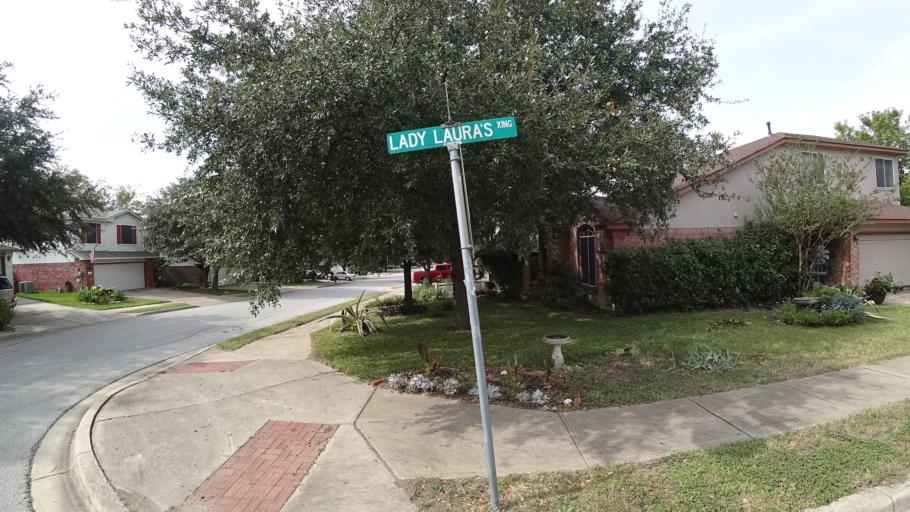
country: US
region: Texas
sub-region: Travis County
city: Windemere
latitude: 30.4457
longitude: -97.6558
